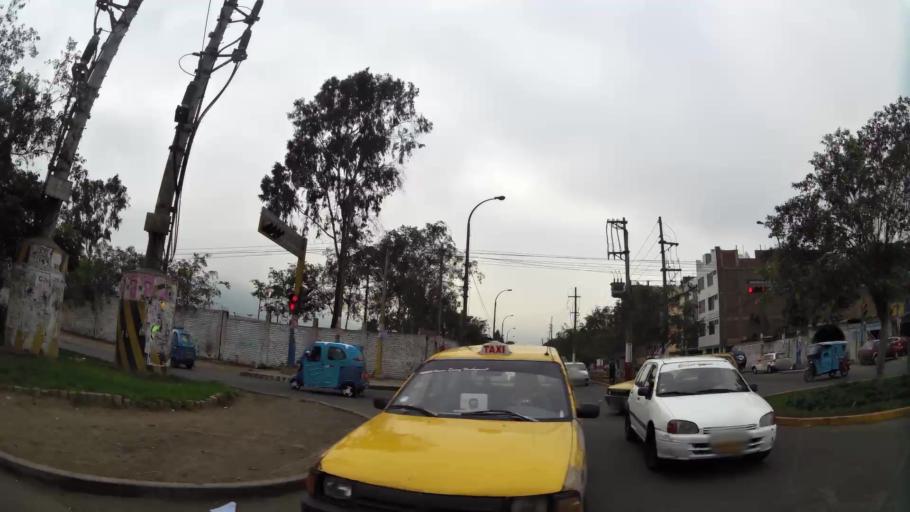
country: PE
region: Lima
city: Lima
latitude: -12.0114
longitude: -76.9985
